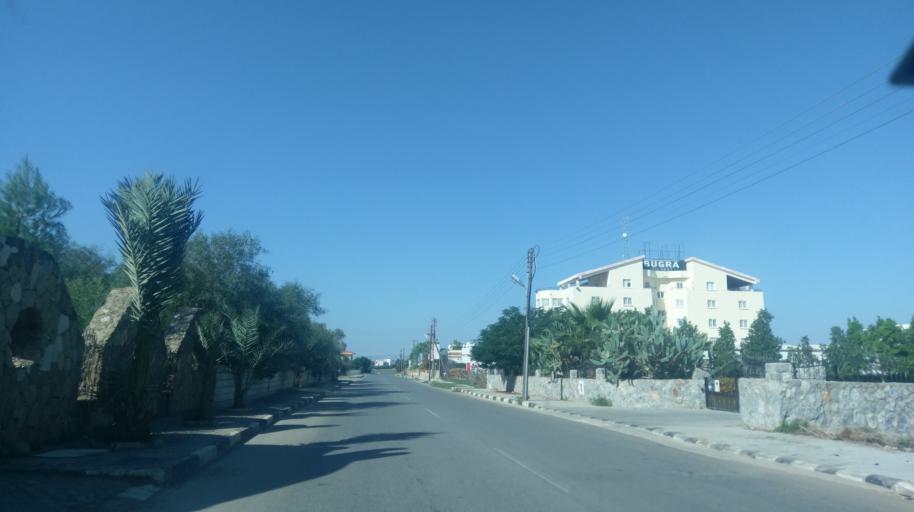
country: CY
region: Ammochostos
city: Famagusta
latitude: 35.1883
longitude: 33.8864
